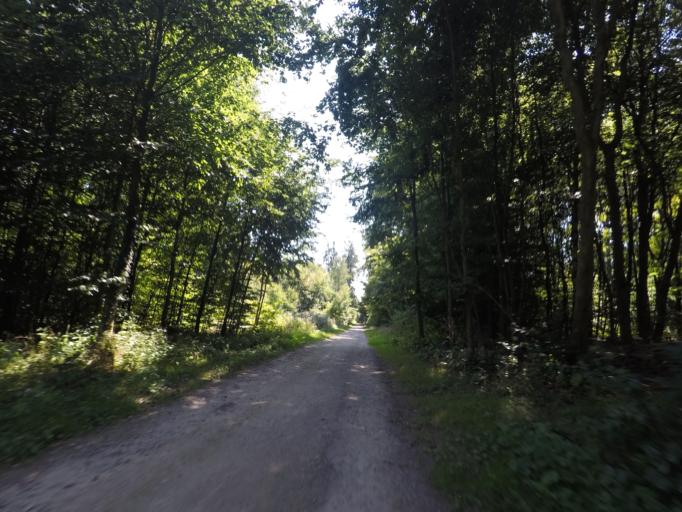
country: LU
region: Luxembourg
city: Bereldange
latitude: 49.6417
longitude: 6.1095
